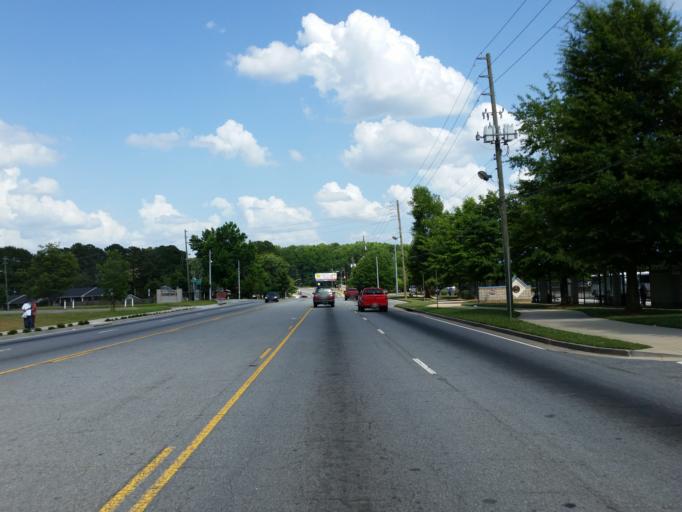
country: US
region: Georgia
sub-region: Cobb County
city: Marietta
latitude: 33.9420
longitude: -84.5299
